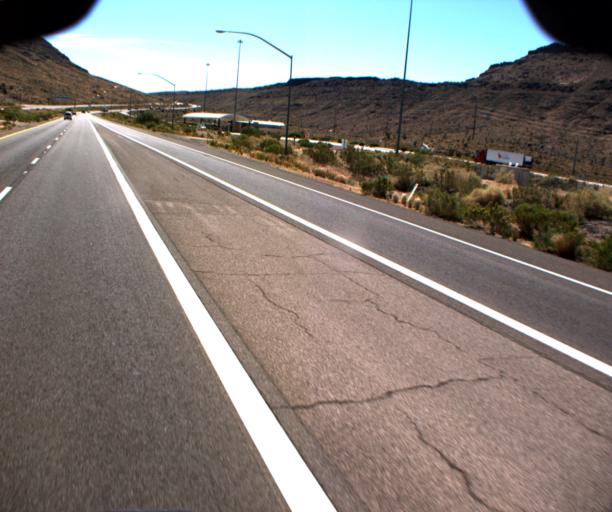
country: US
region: Arizona
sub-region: Mohave County
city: Kingman
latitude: 35.2196
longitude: -114.1225
